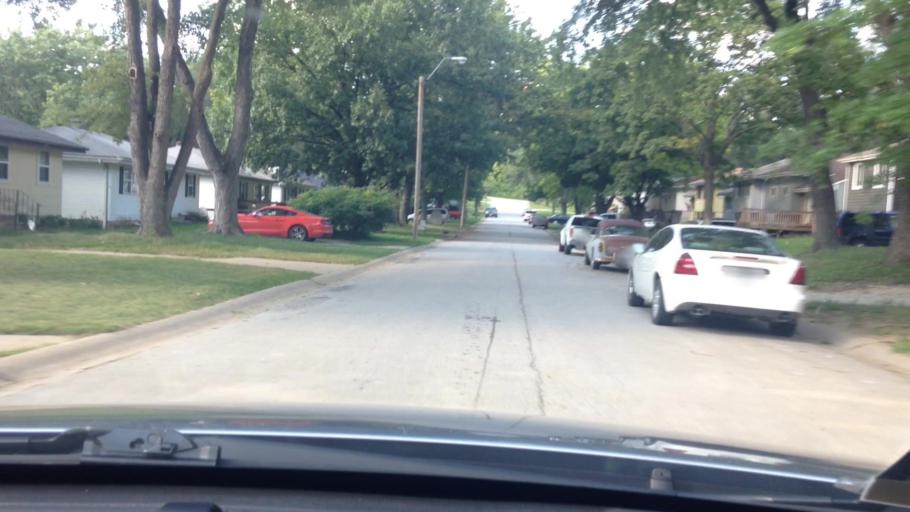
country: US
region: Missouri
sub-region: Clay County
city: Claycomo
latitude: 39.1786
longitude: -94.4978
